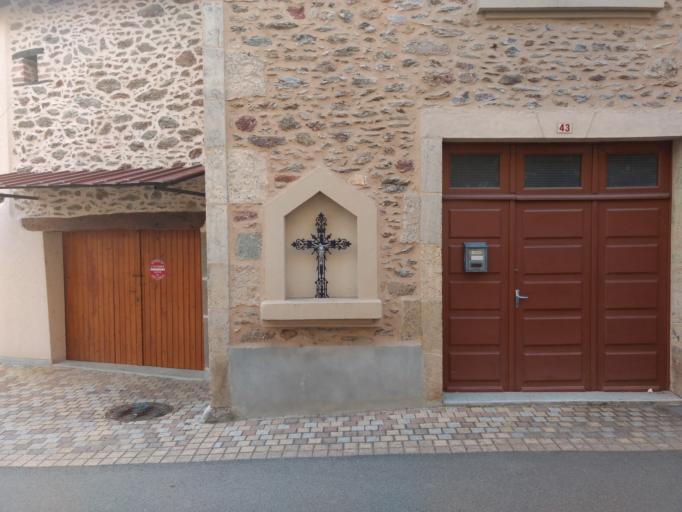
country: FR
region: Midi-Pyrenees
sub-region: Departement de l'Aveyron
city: Livinhac-le-Haut
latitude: 44.6055
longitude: 2.2491
